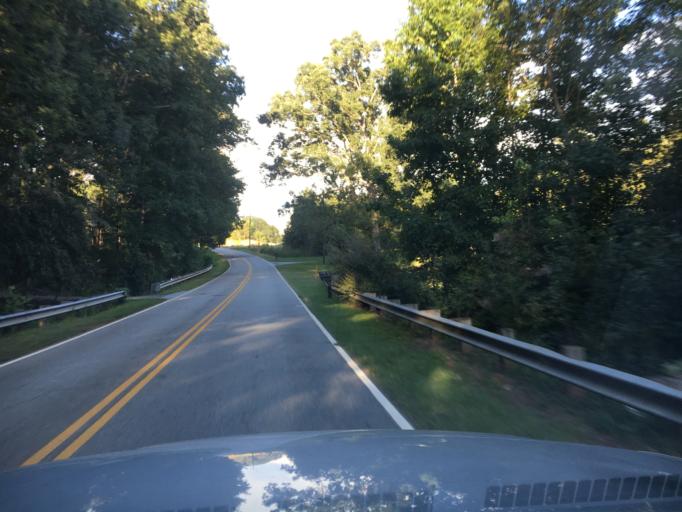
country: US
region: South Carolina
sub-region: Spartanburg County
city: Roebuck
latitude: 34.8862
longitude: -81.9997
